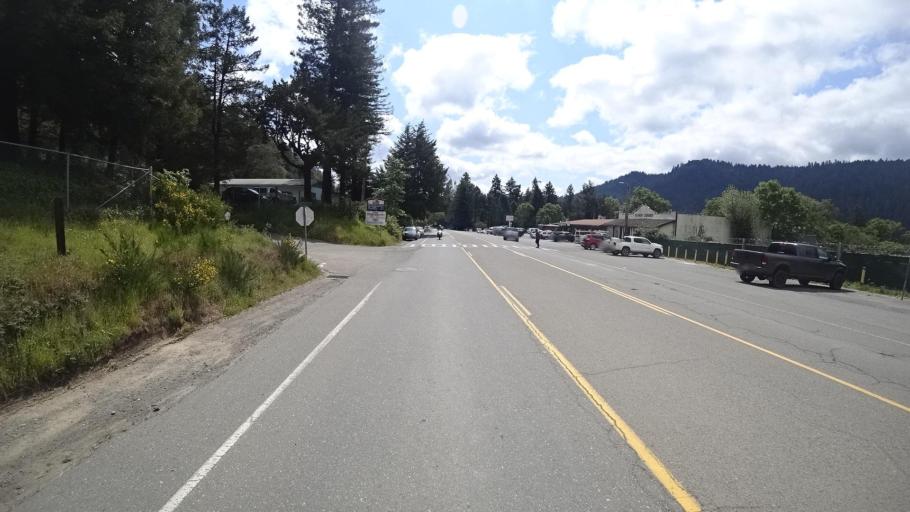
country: US
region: California
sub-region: Humboldt County
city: Redway
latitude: 40.1200
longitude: -123.8228
